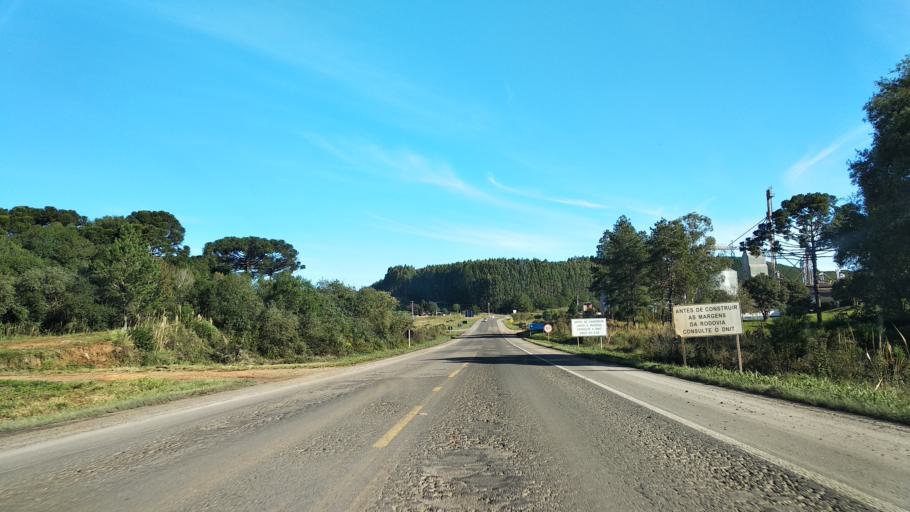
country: BR
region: Santa Catarina
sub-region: Campos Novos
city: Campos Novos
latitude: -27.3954
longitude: -51.1932
